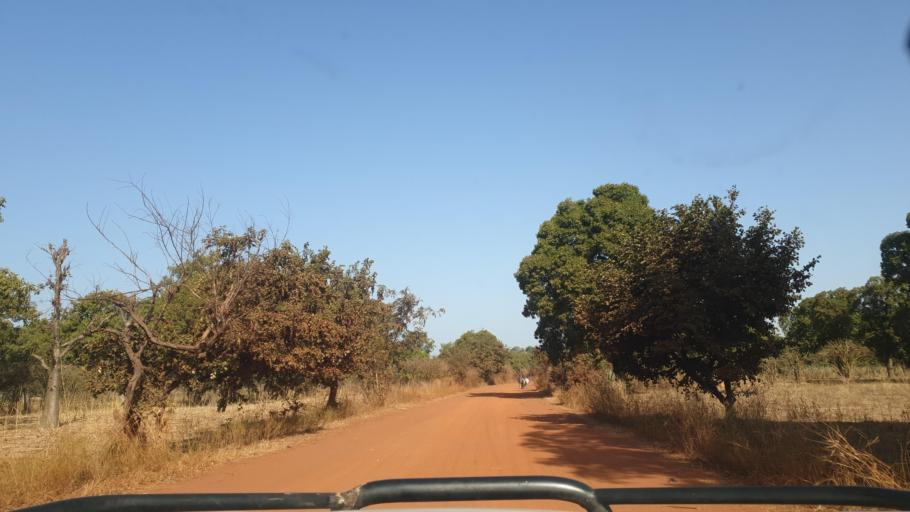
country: ML
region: Sikasso
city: Kolondieba
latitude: 11.7365
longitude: -6.8936
